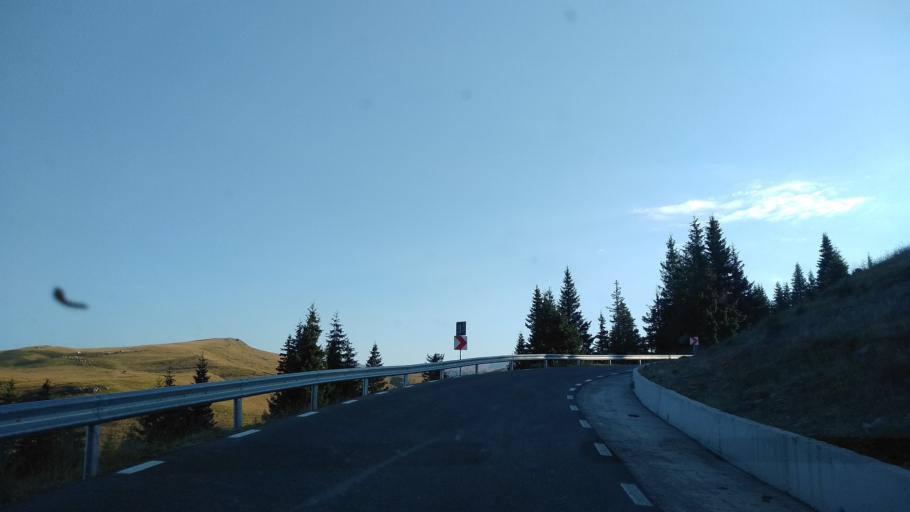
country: RO
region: Prahova
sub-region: Oras Sinaia
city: Sinaia
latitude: 45.3385
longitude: 25.4605
